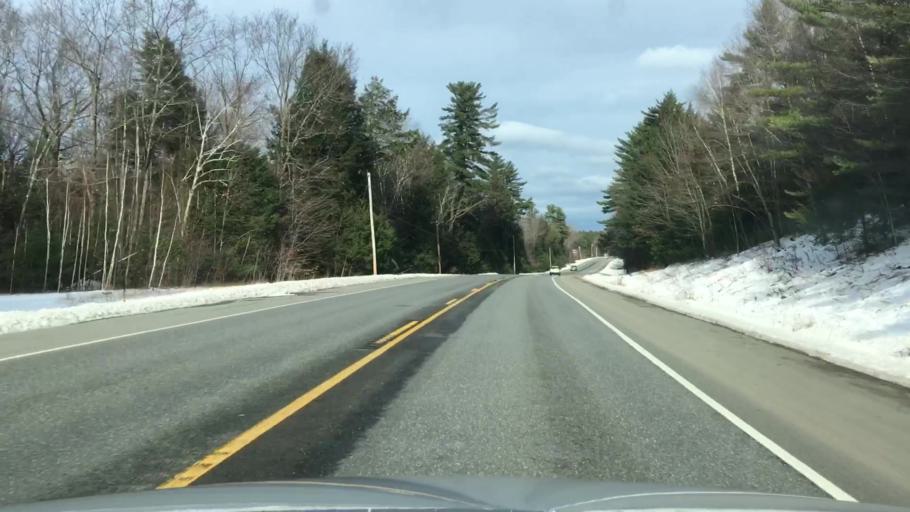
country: US
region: Maine
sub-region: Kennebec County
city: Monmouth
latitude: 44.2478
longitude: -70.0656
